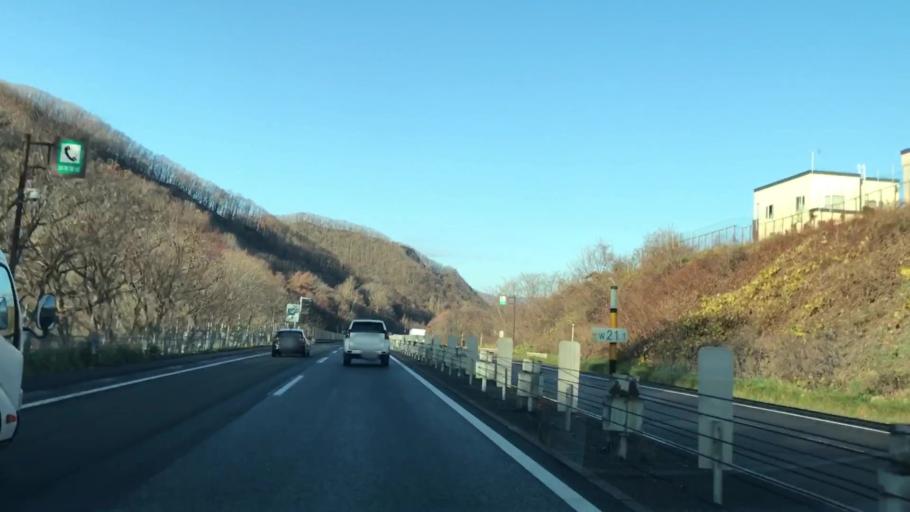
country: JP
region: Hokkaido
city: Sapporo
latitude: 43.1257
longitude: 141.2023
